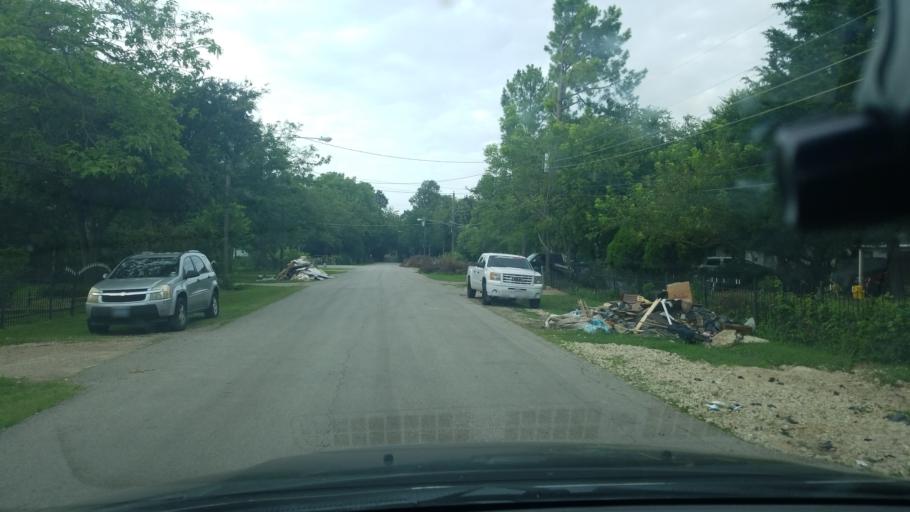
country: US
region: Texas
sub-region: Dallas County
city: Balch Springs
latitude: 32.7334
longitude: -96.6689
